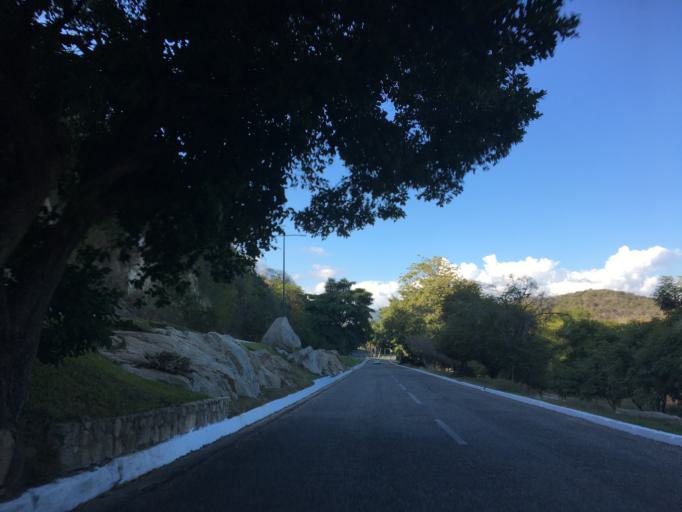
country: MX
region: Oaxaca
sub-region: Santa Maria Huatulco
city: Crucecita
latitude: 15.7708
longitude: -96.1022
